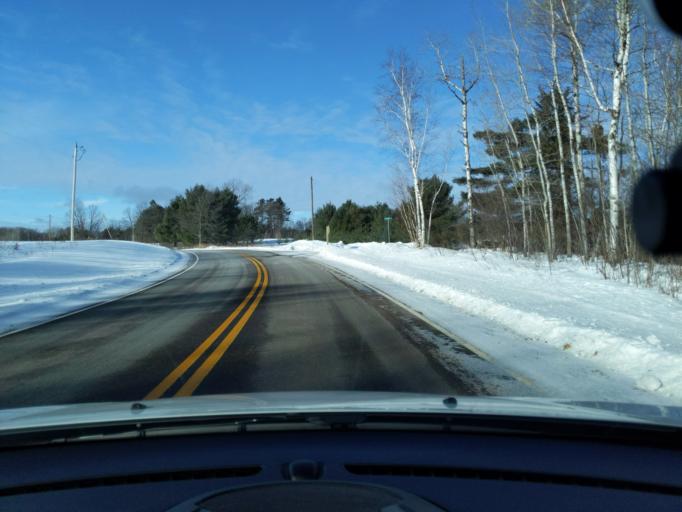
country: US
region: Wisconsin
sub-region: Sawyer County
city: Little Round Lake
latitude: 46.1134
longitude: -91.3171
